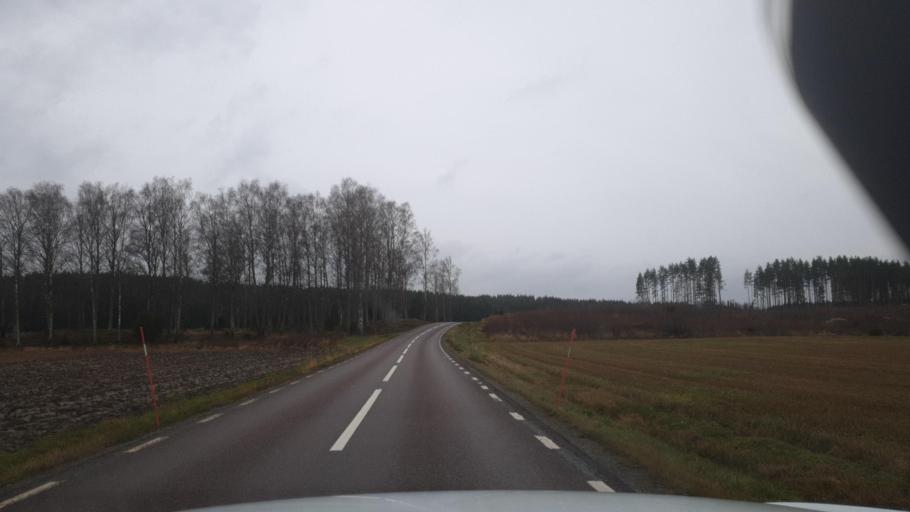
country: SE
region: Vaermland
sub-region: Arvika Kommun
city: Arvika
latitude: 59.5892
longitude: 12.5417
